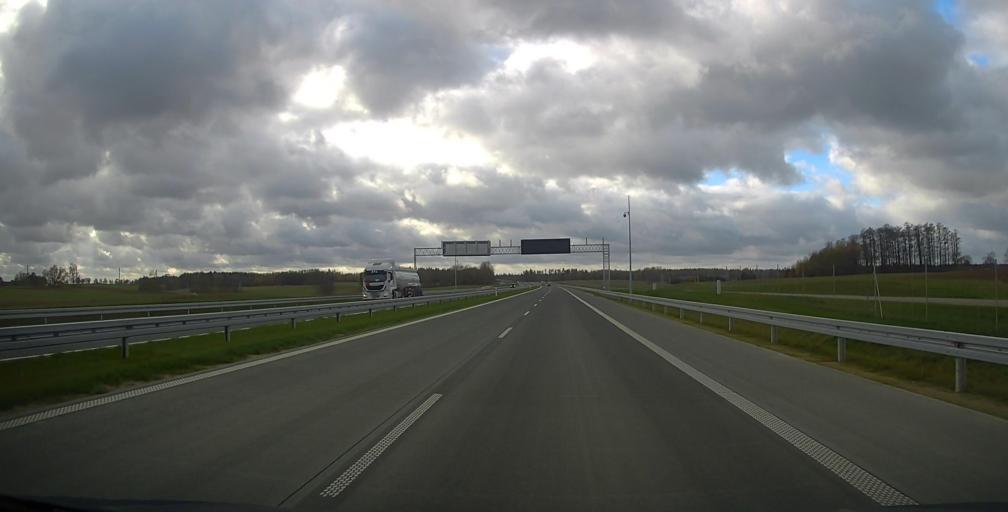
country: PL
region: Podlasie
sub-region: Powiat suwalski
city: Raczki
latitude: 53.9088
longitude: 22.7131
